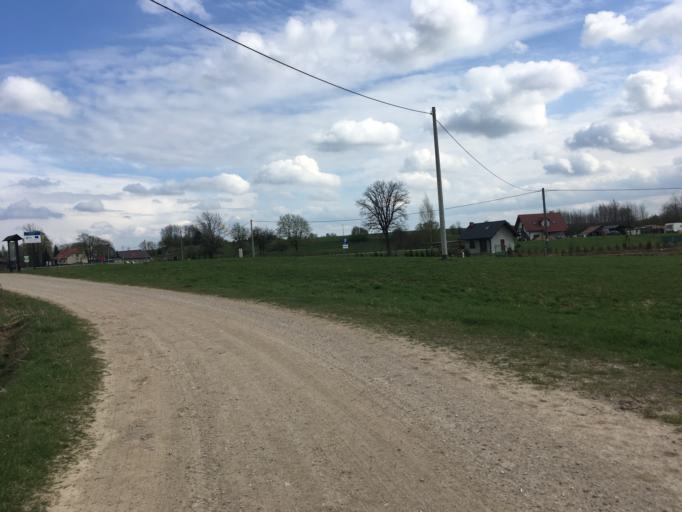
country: PL
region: Podlasie
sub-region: Powiat suwalski
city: Filipow
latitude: 54.3628
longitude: 22.7947
